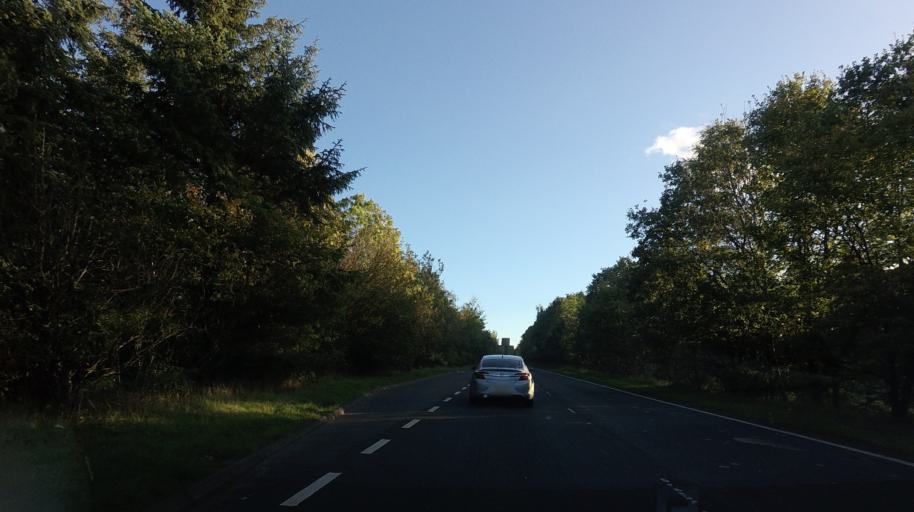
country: GB
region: Scotland
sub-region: Falkirk
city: Polmont
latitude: 55.9772
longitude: -3.6848
